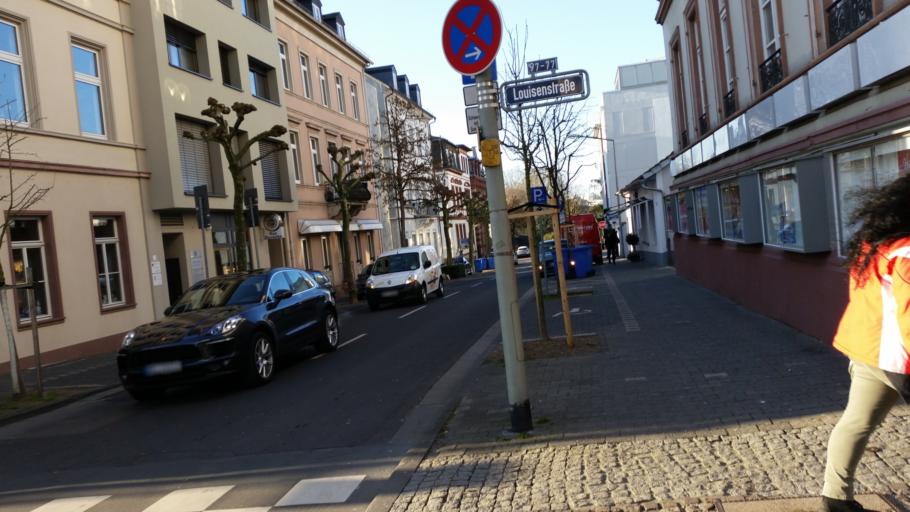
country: DE
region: Hesse
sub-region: Regierungsbezirk Darmstadt
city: Bad Homburg vor der Hoehe
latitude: 50.2252
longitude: 8.6203
